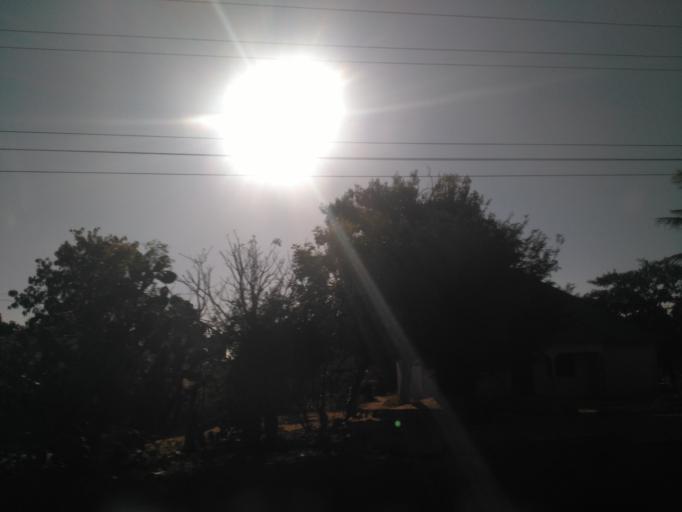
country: TZ
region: Dodoma
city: Dodoma
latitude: -6.1441
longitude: 35.7470
